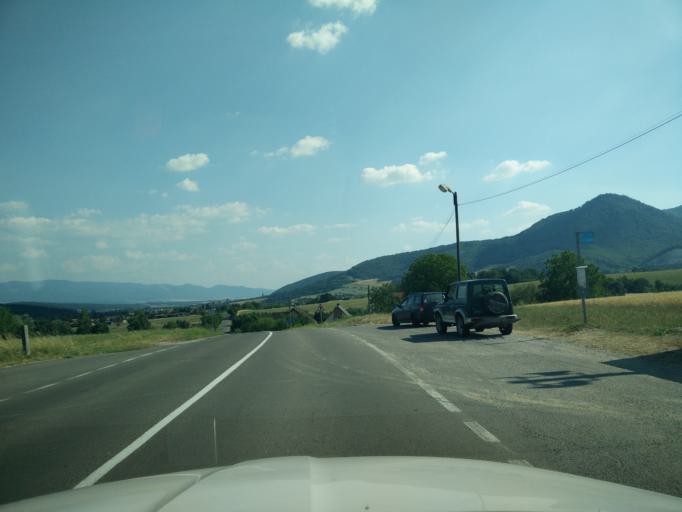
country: SK
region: Nitriansky
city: Novaky
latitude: 48.8072
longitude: 18.4745
